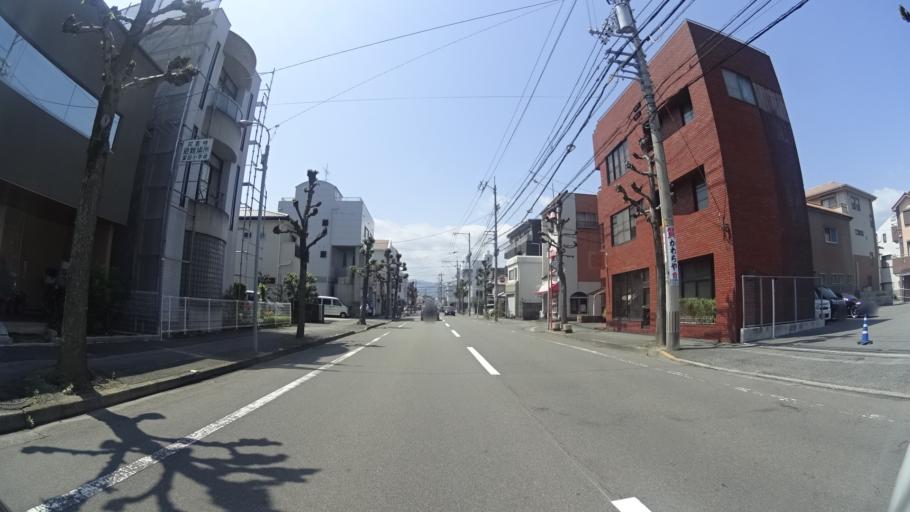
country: JP
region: Tokushima
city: Tokushima-shi
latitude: 34.0612
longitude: 134.5518
